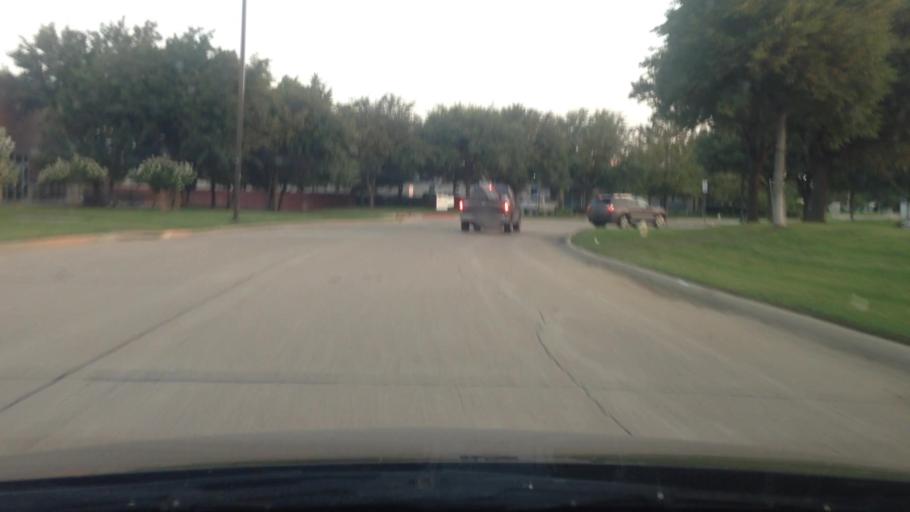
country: US
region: Texas
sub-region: Dallas County
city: Coppell
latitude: 32.9364
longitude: -96.9978
